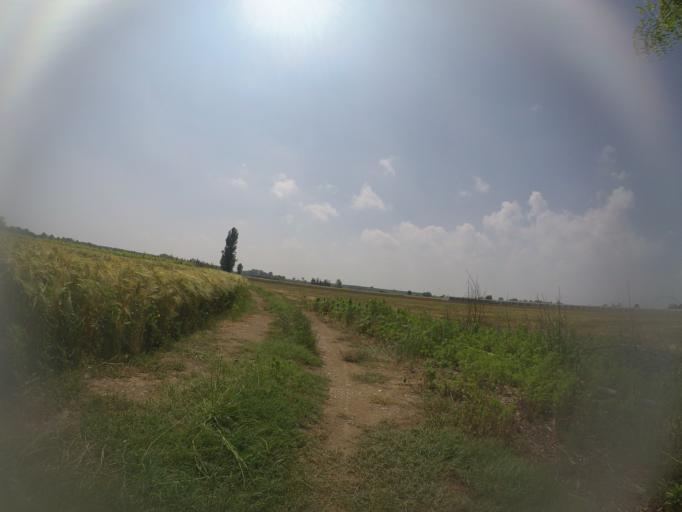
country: IT
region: Friuli Venezia Giulia
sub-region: Provincia di Udine
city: Bertiolo
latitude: 45.9353
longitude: 13.0429
